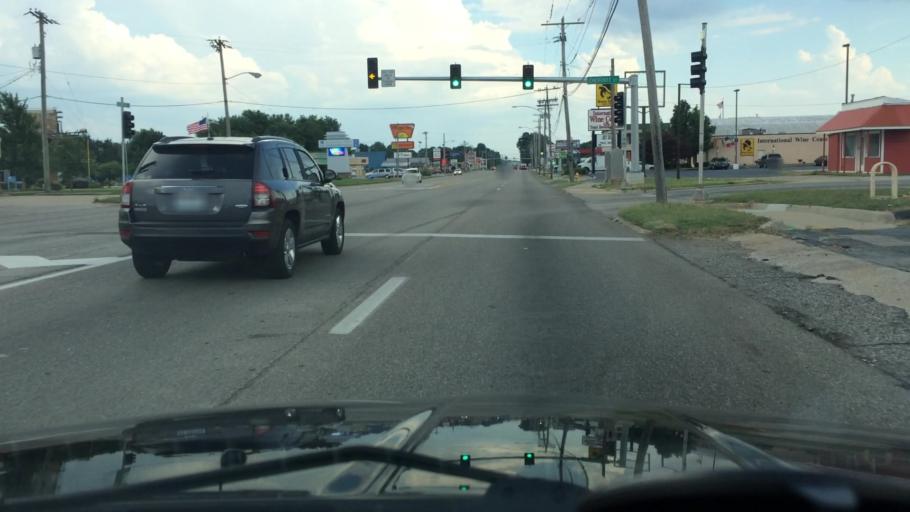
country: US
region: Missouri
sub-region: Greene County
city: Springfield
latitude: 37.1786
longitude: -93.2625
